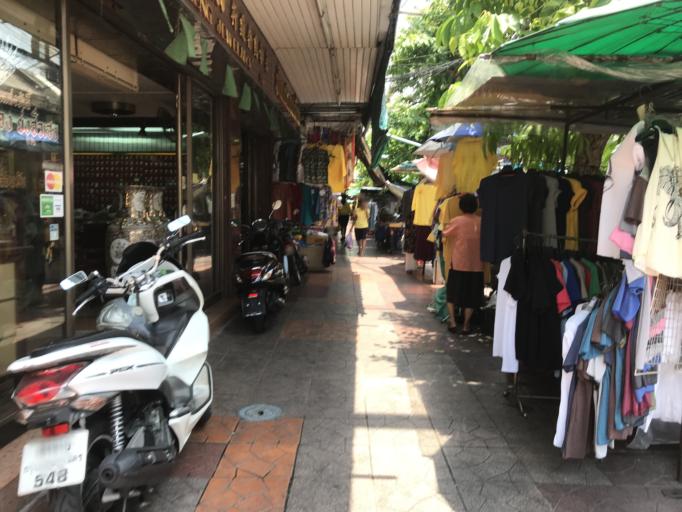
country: TH
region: Bangkok
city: Phra Nakhon
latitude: 13.7619
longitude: 100.4982
